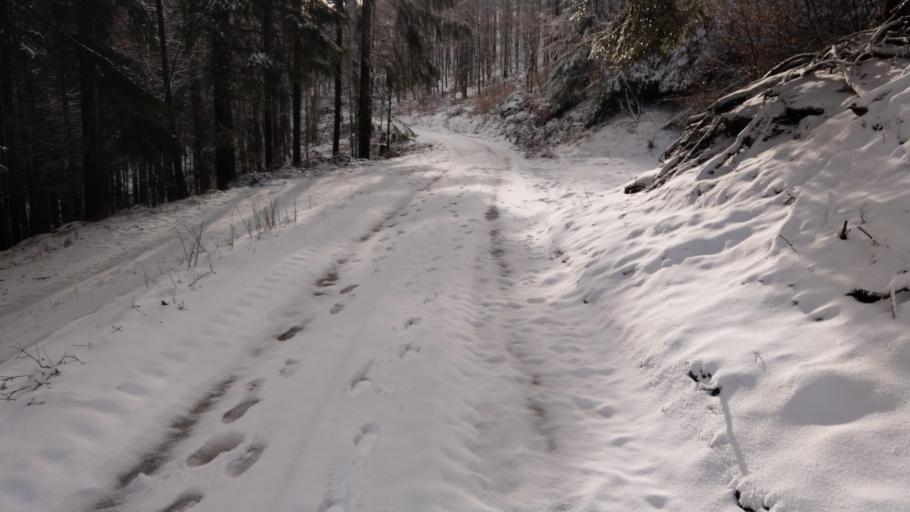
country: DE
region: Hesse
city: Willingen
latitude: 51.3136
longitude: 8.5801
